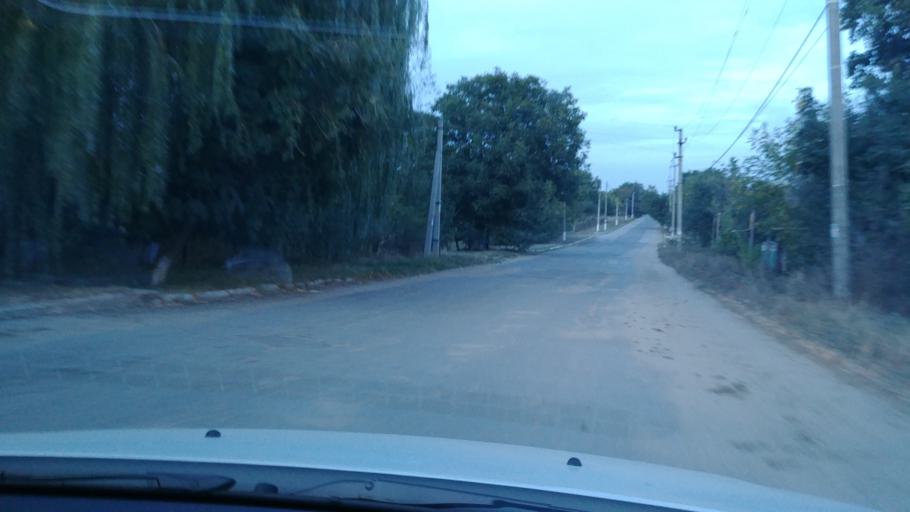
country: MD
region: Rezina
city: Saharna
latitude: 47.6757
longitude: 28.9598
